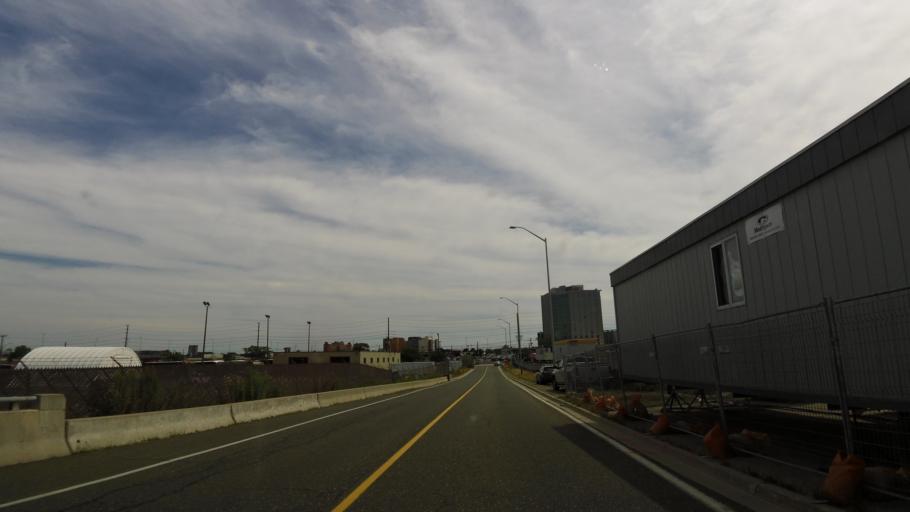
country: CA
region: Ontario
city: Etobicoke
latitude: 43.6926
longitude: -79.6093
